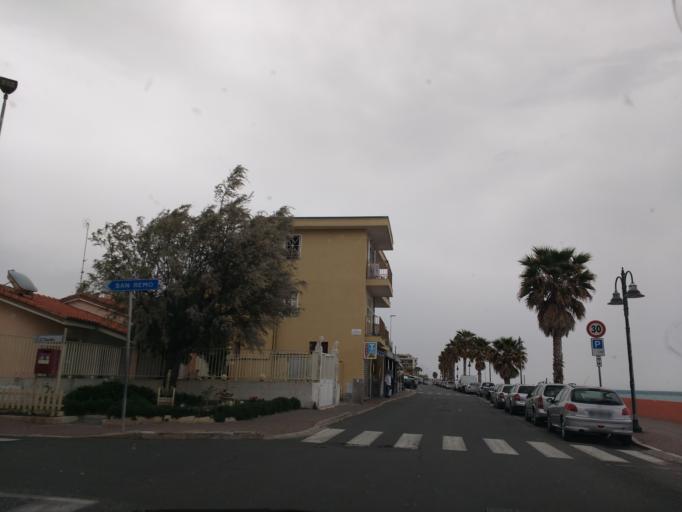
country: IT
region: Liguria
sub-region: Provincia di Imperia
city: Ventimiglia
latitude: 43.7857
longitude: 7.6201
